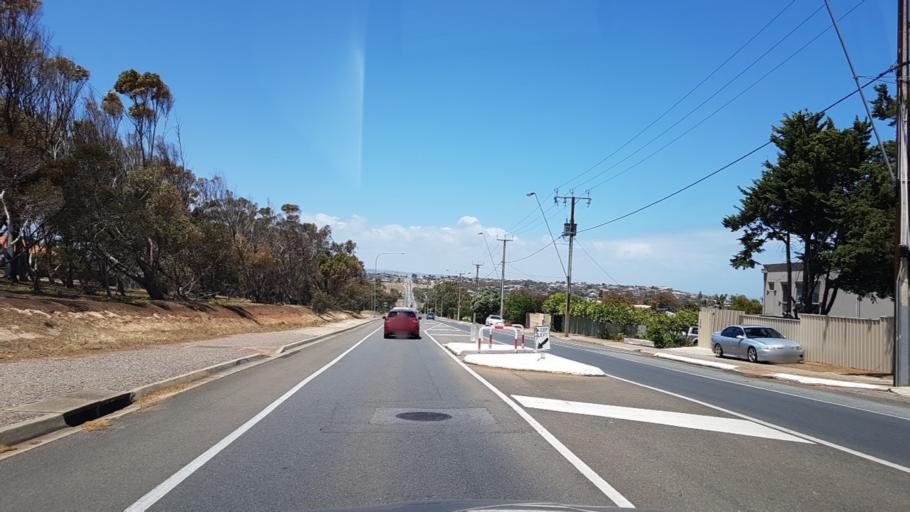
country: AU
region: South Australia
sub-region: Onkaparinga
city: Moana
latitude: -35.1971
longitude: 138.4781
